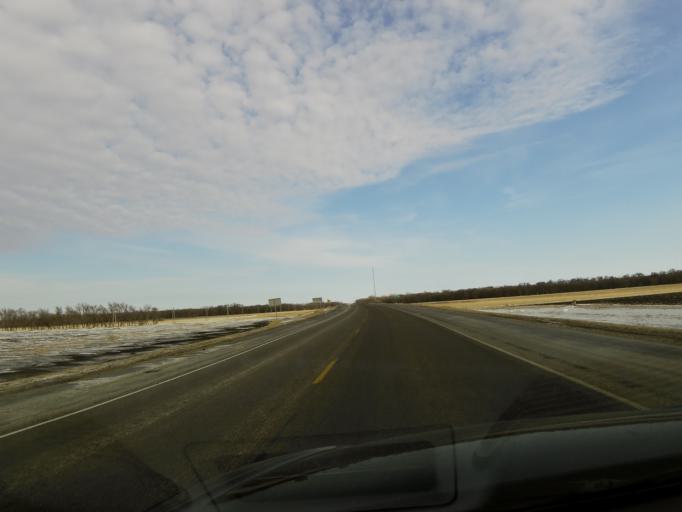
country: US
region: North Dakota
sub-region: Walsh County
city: Grafton
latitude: 48.5714
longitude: -97.1650
